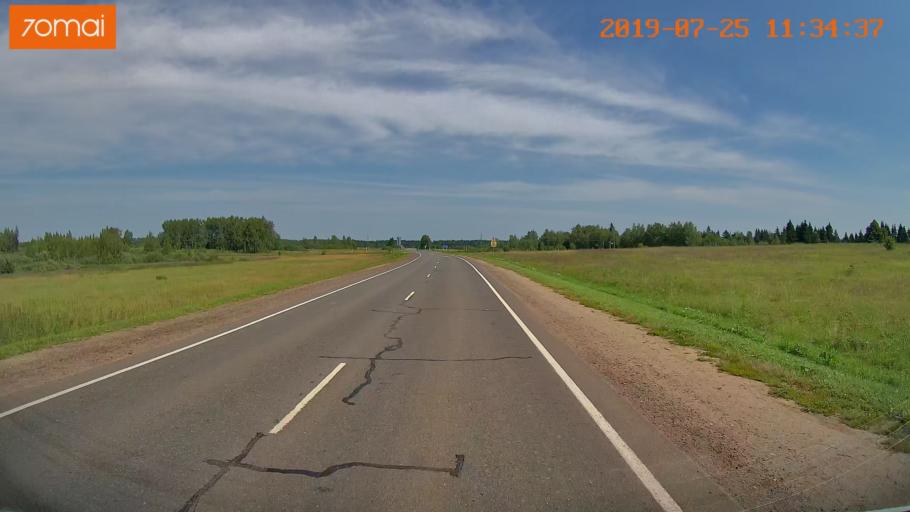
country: RU
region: Ivanovo
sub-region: Privolzhskiy Rayon
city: Ples
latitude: 57.4014
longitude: 41.4161
